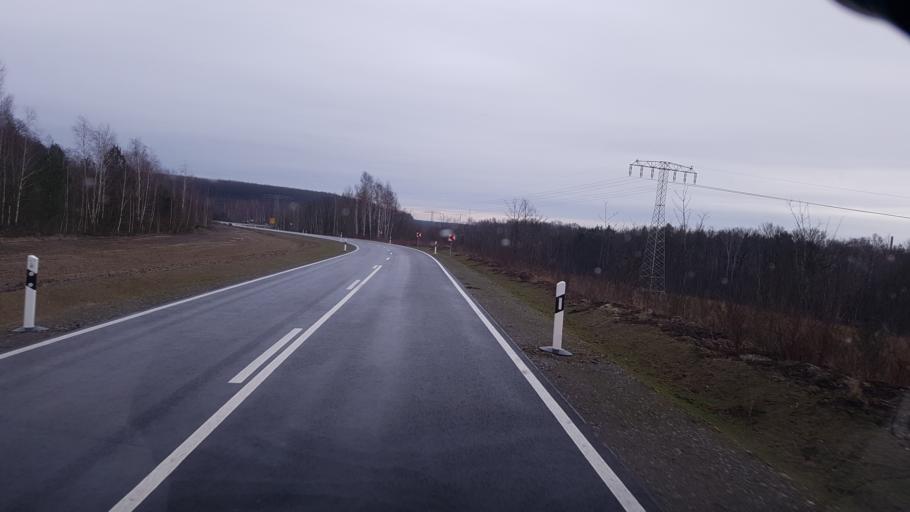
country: DE
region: Brandenburg
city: Lauchhammer
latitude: 51.5136
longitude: 13.7979
